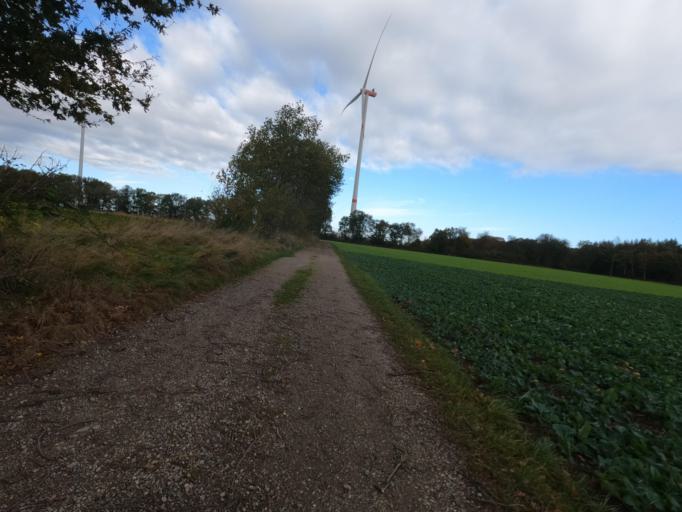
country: DE
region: North Rhine-Westphalia
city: Huckelhoven
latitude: 51.0606
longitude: 6.2549
